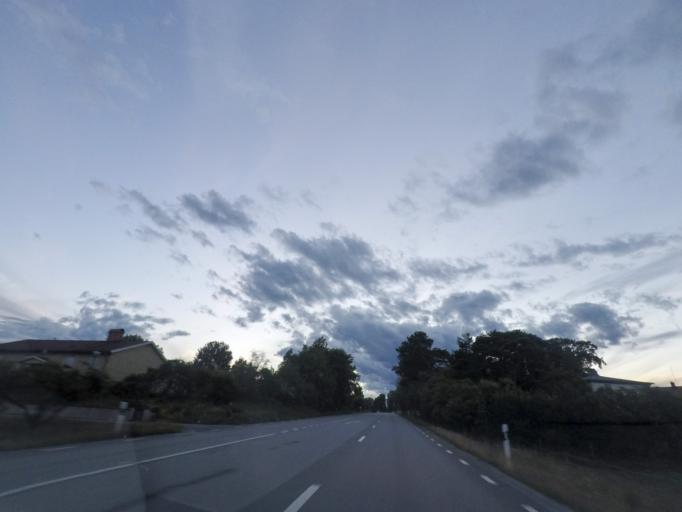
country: SE
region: Uppsala
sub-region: Habo Kommun
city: Balsta
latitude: 59.6289
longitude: 17.4873
